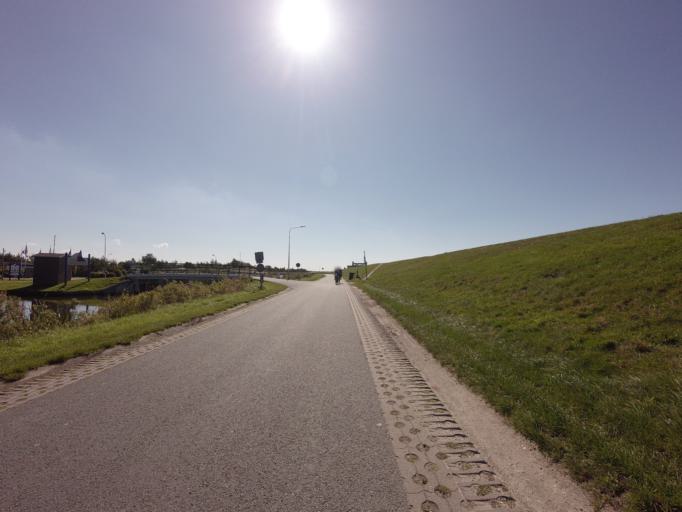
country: NL
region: Friesland
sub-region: Sudwest Fryslan
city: Koudum
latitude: 52.9353
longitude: 5.4033
